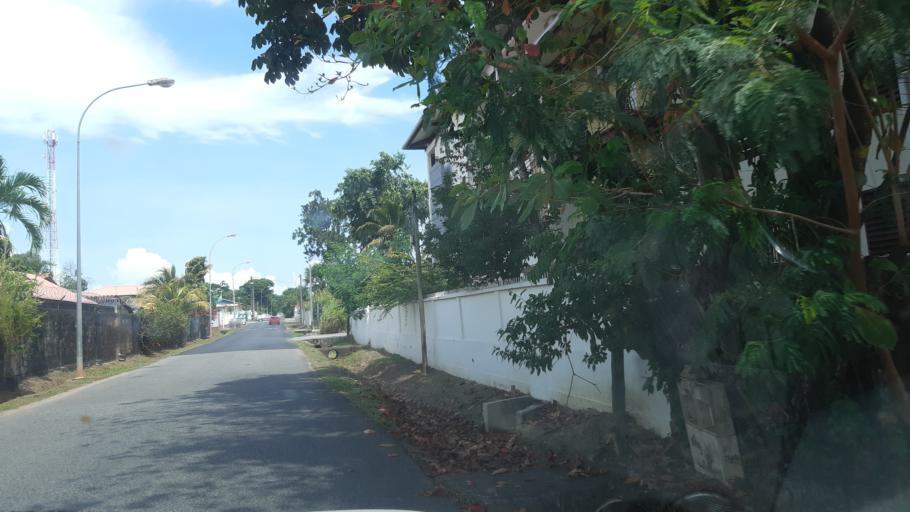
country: GF
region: Guyane
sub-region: Guyane
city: Remire-Montjoly
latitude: 4.9310
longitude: -52.2980
